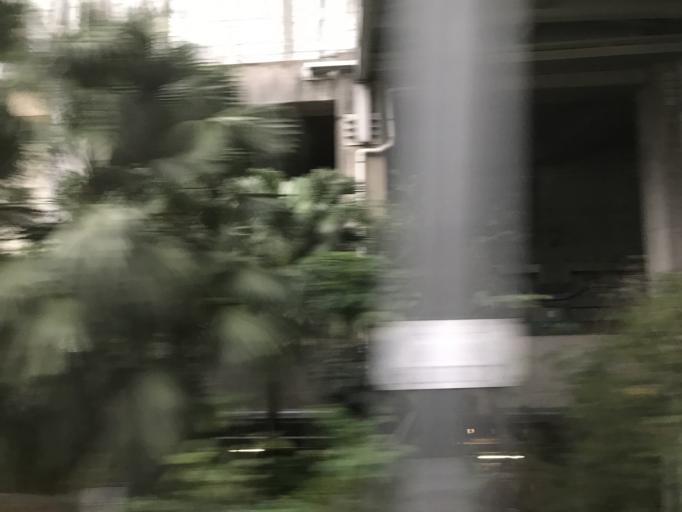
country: HK
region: Sha Tin
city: Sha Tin
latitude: 22.3721
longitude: 114.1772
